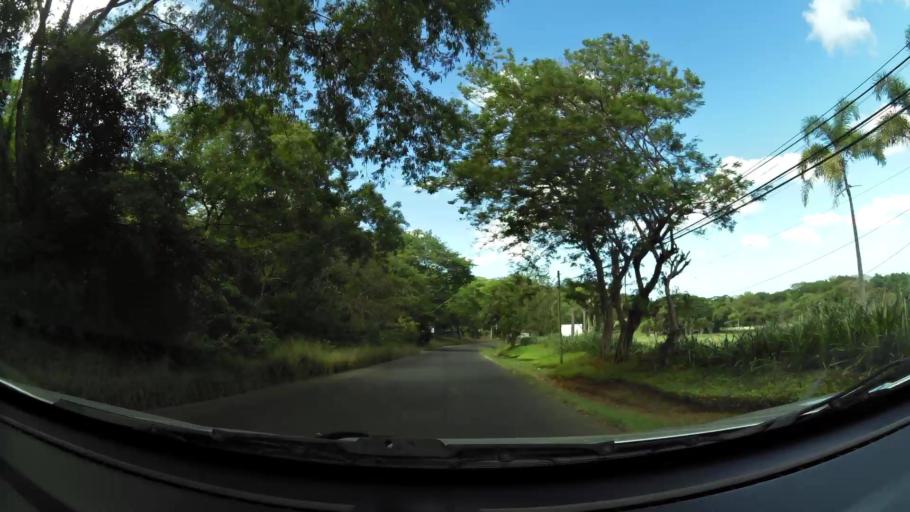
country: CR
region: Guanacaste
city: Santa Cruz
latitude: 10.3096
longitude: -85.8135
